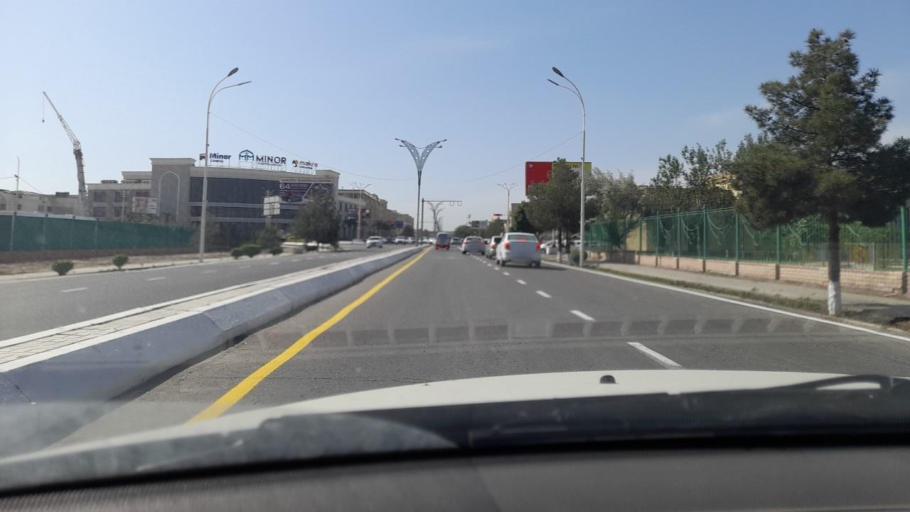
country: UZ
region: Bukhara
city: Bukhara
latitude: 39.7823
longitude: 64.4295
